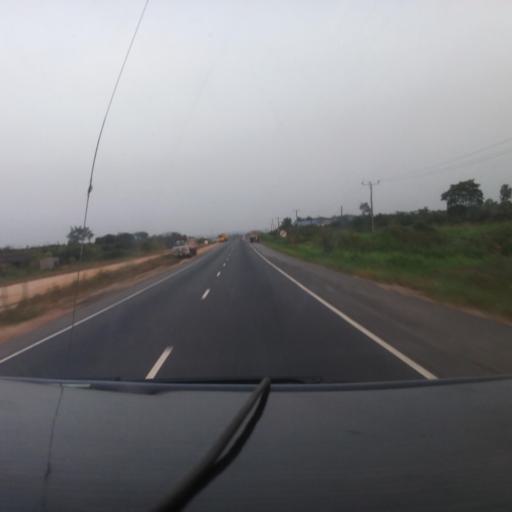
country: GH
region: Eastern
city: Nsawam
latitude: 5.8722
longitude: -0.3688
